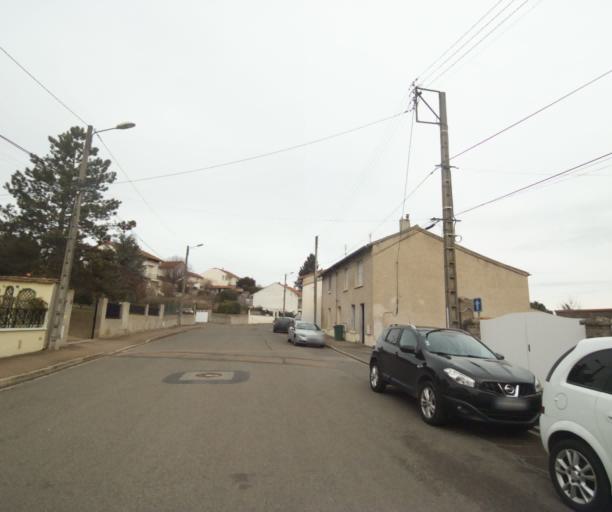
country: FR
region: Rhone-Alpes
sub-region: Departement de la Loire
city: Roanne
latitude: 46.0246
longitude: 4.0609
